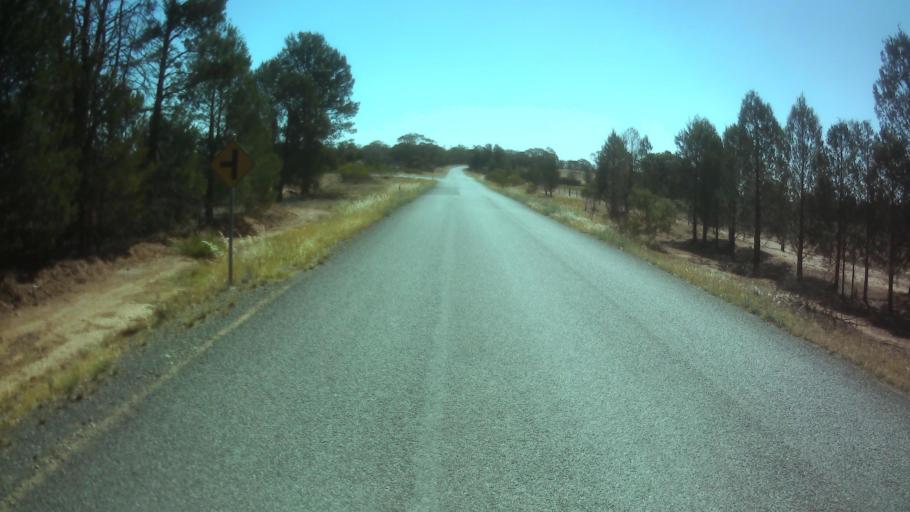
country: AU
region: New South Wales
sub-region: Weddin
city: Grenfell
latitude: -33.7550
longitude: 147.8320
